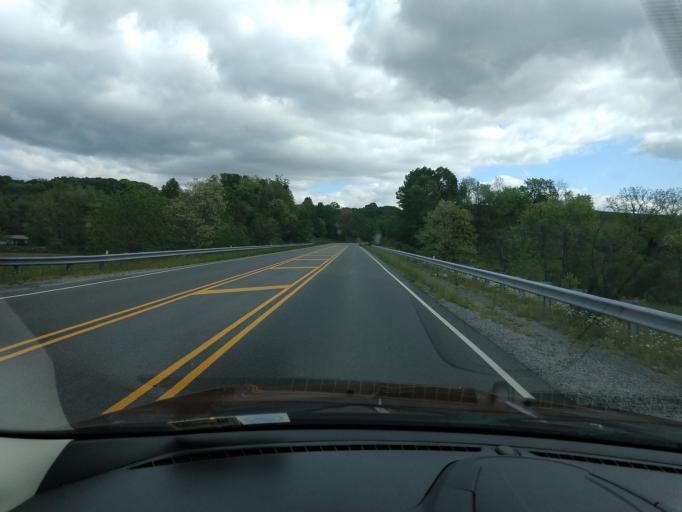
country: US
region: Virginia
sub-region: Wythe County
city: Wytheville
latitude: 36.8892
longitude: -80.9753
